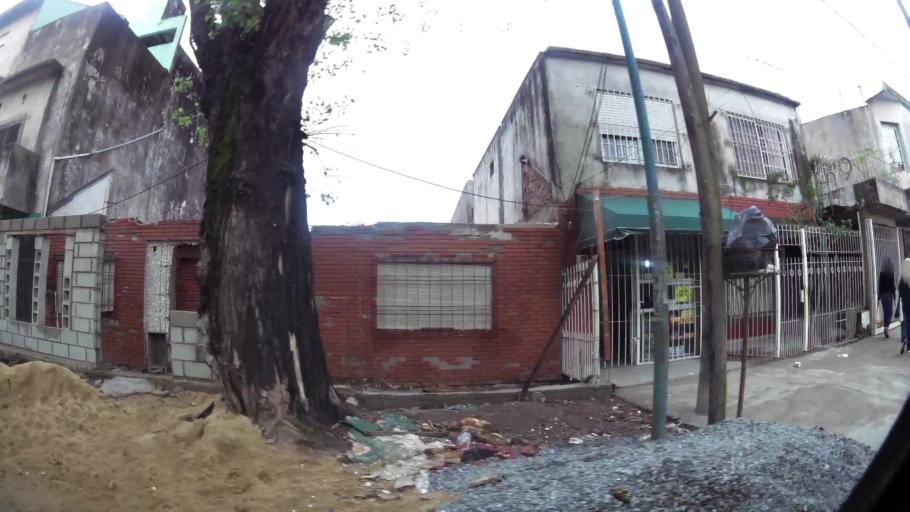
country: AR
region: Buenos Aires
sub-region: Partido de Lanus
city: Lanus
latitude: -34.7239
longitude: -58.3393
